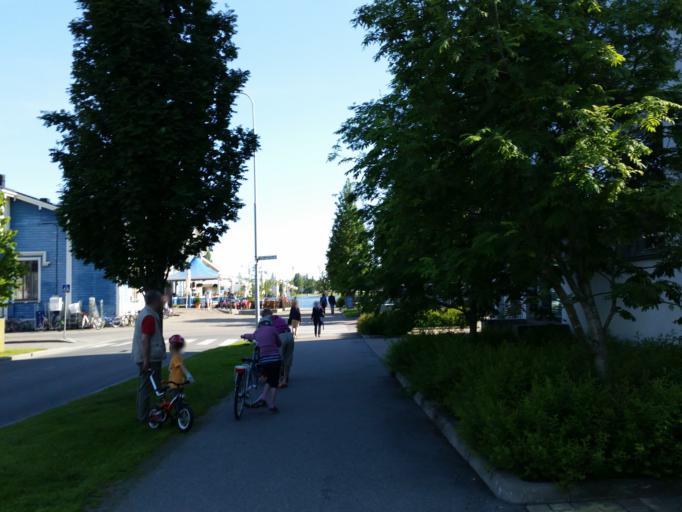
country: FI
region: Northern Savo
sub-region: Kuopio
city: Kuopio
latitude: 62.8929
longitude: 27.6962
